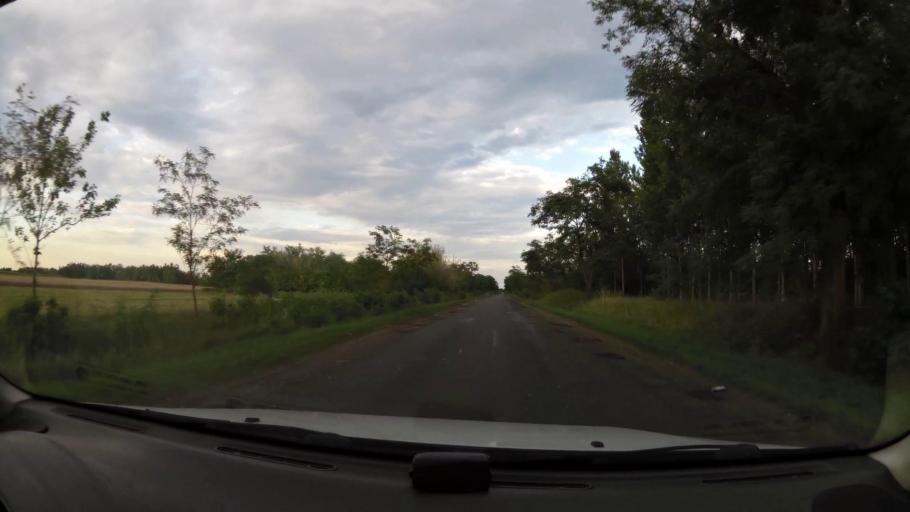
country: HU
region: Pest
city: Tapioszolos
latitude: 47.3206
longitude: 19.8411
